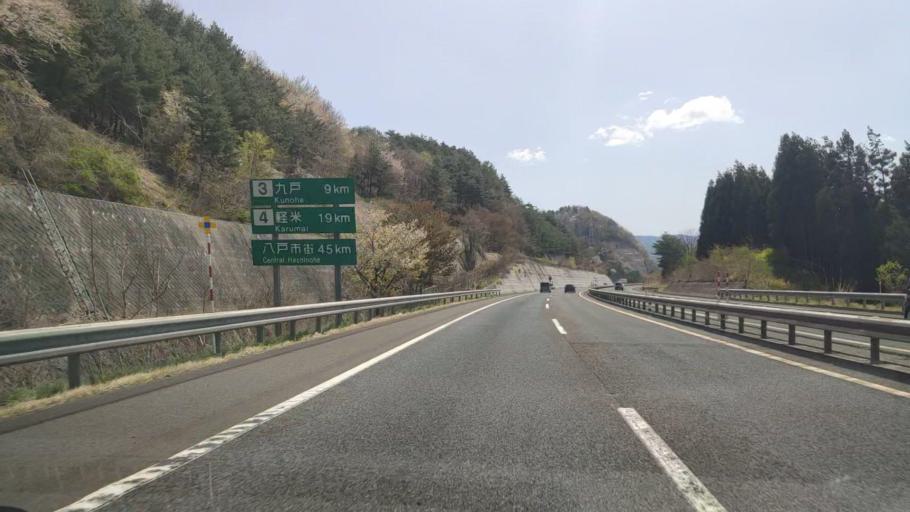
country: JP
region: Iwate
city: Ichinohe
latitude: 40.2287
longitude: 141.3217
